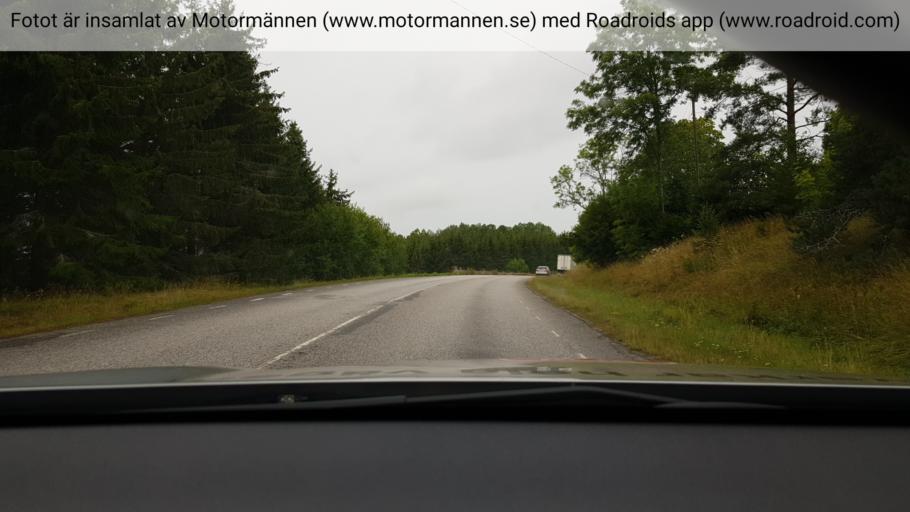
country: SE
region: Soedermanland
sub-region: Strangnas Kommun
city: Mariefred
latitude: 59.2211
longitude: 17.2303
